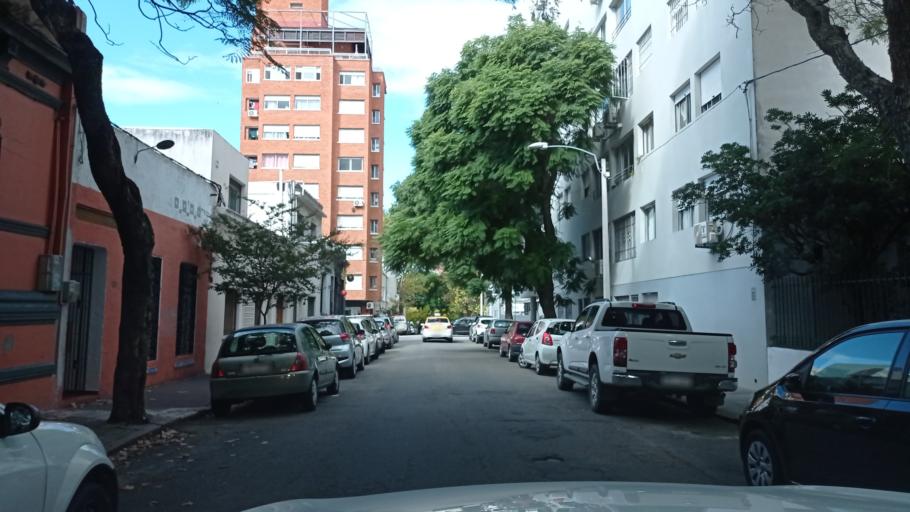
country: UY
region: Montevideo
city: Montevideo
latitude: -34.9039
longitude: -56.1527
